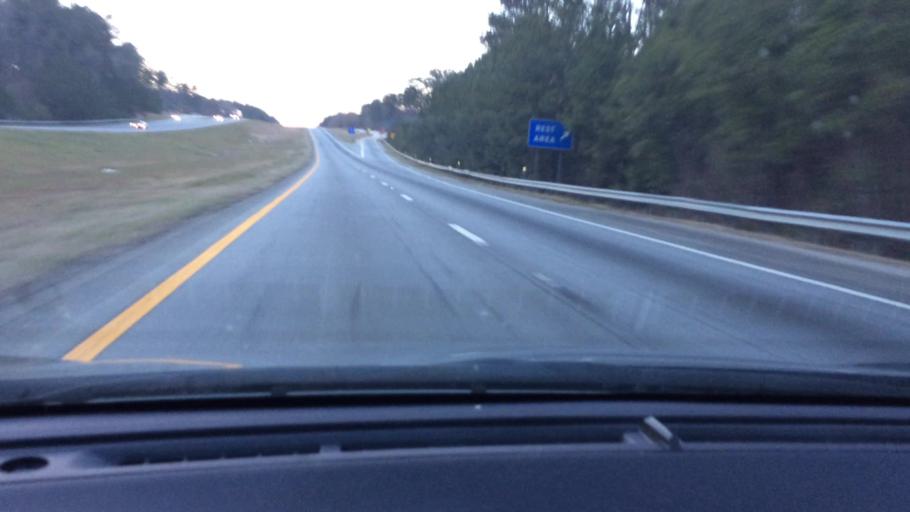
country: US
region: South Carolina
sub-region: Laurens County
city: Joanna
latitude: 34.4090
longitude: -81.7011
